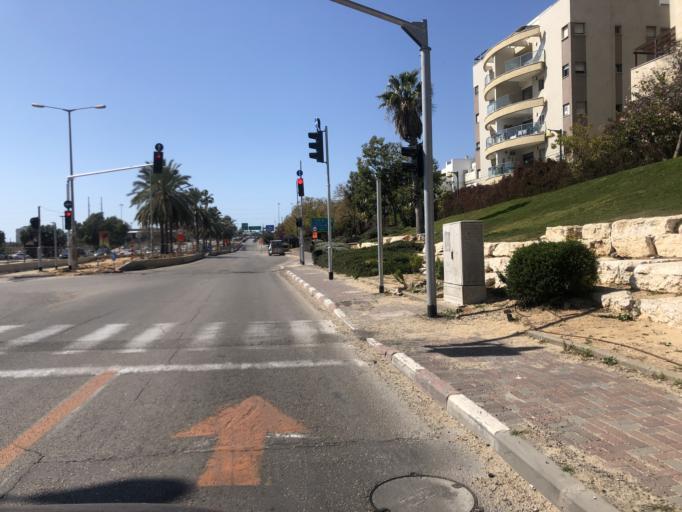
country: IL
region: Tel Aviv
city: Holon
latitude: 32.0012
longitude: 34.7641
